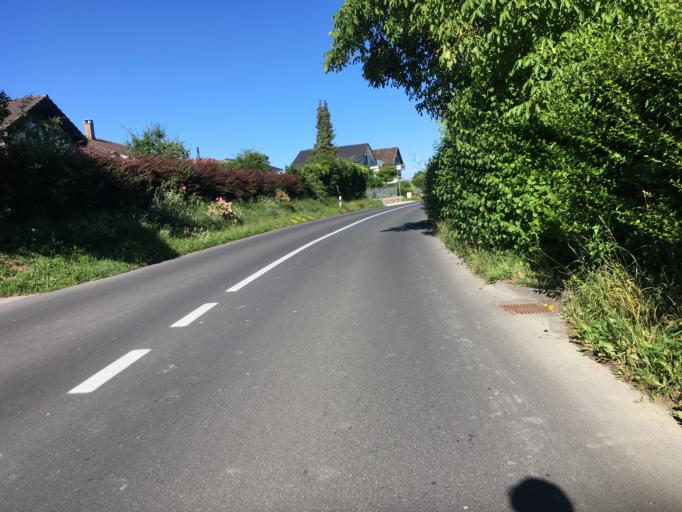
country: CH
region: Fribourg
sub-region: See District
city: Bas-Vully
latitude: 46.9434
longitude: 7.0676
